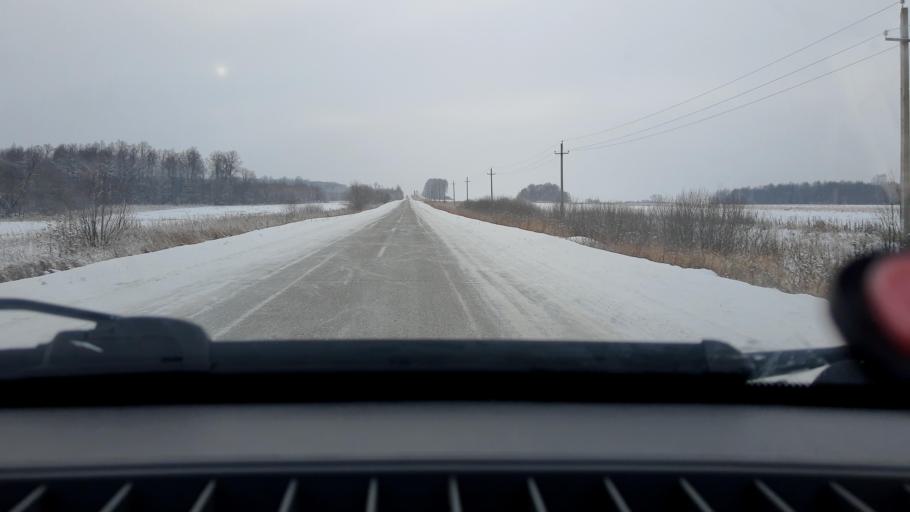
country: RU
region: Bashkortostan
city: Iglino
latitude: 54.6710
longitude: 56.4205
